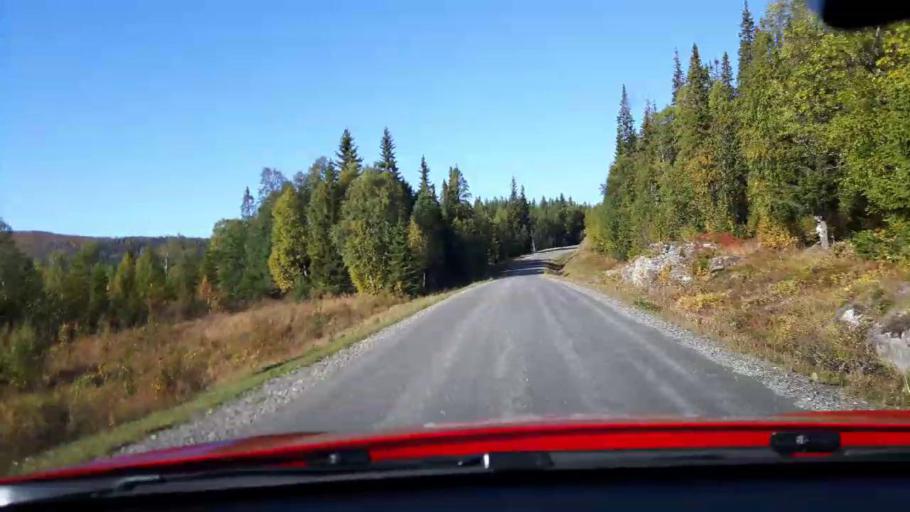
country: NO
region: Nord-Trondelag
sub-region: Lierne
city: Sandvika
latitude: 64.6074
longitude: 13.7136
